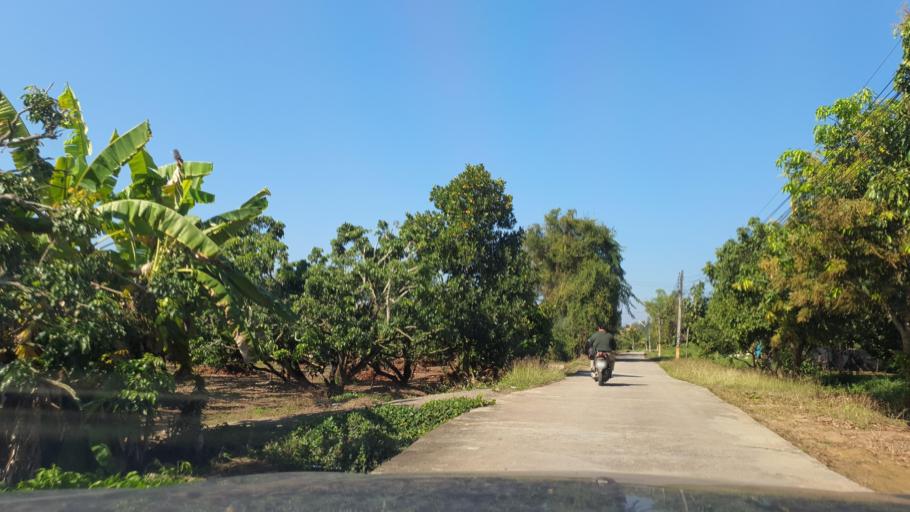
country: TH
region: Chiang Mai
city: Saraphi
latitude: 18.7023
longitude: 99.0744
